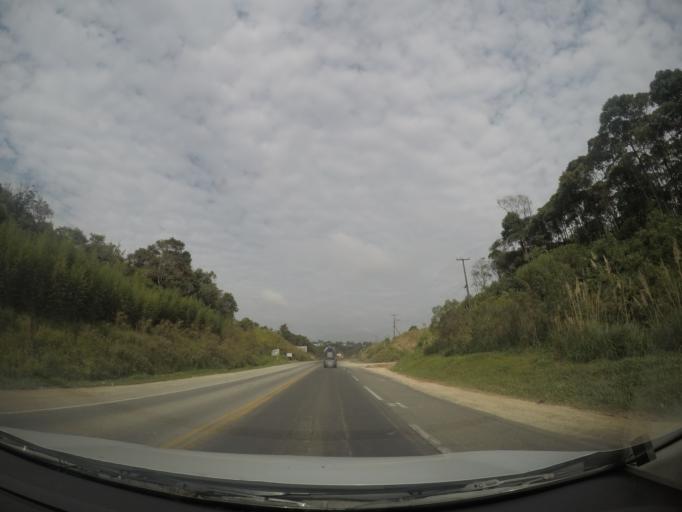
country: BR
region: Parana
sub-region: Colombo
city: Colombo
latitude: -25.3370
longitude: -49.2559
